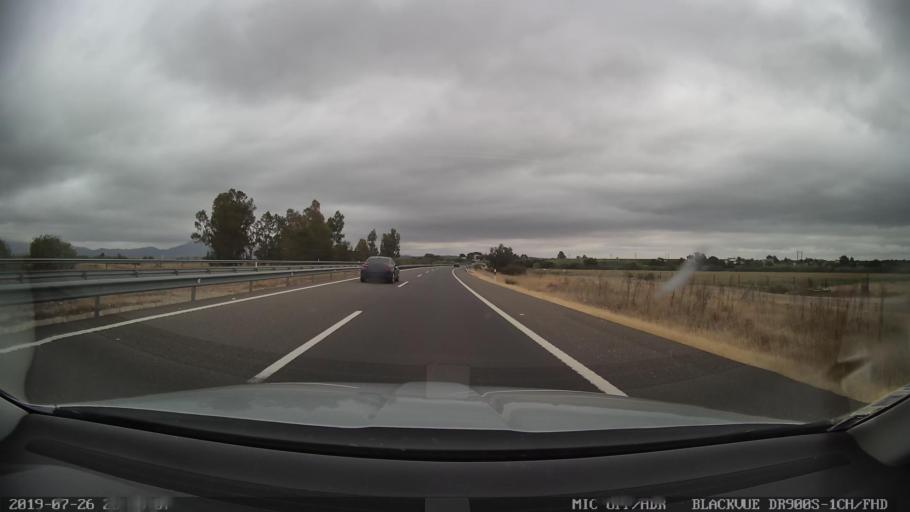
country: ES
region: Extremadura
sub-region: Provincia de Badajoz
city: Santa Amalia
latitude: 39.0907
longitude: -6.0179
